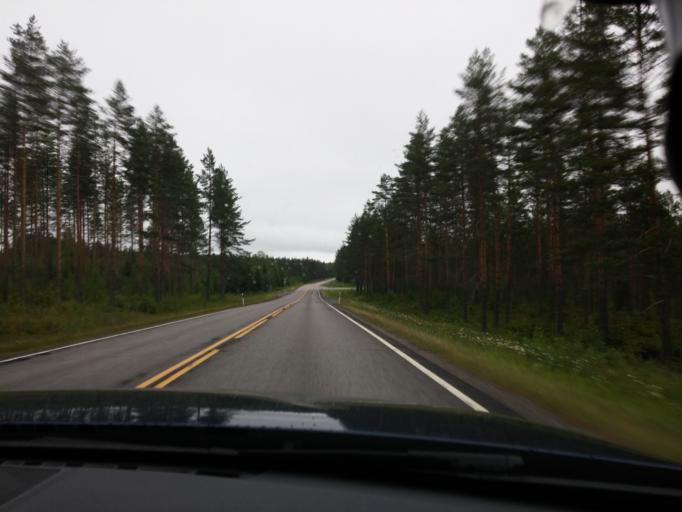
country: FI
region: Pirkanmaa
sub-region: Ylae-Pirkanmaa
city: Vilppula
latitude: 61.9113
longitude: 24.5278
